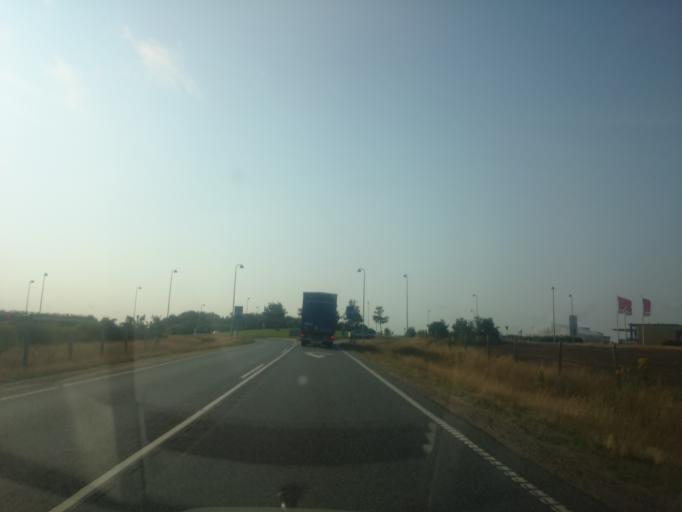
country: DK
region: South Denmark
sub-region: Billund Kommune
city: Billund
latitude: 55.7147
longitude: 9.2187
